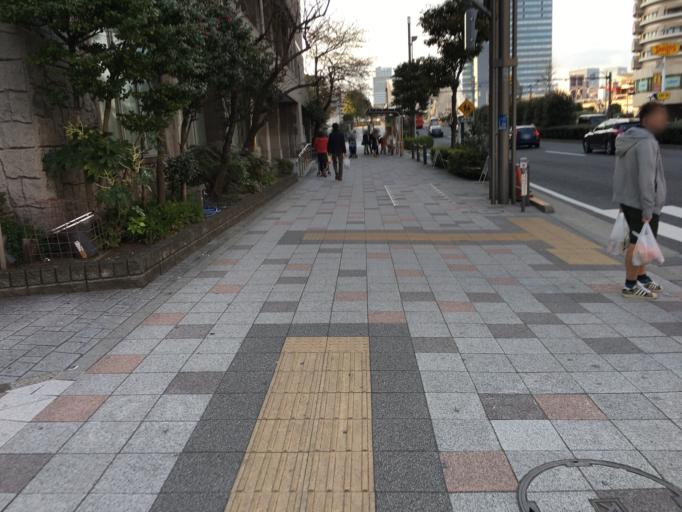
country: JP
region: Tokyo
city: Tokyo
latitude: 35.6600
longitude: 139.7768
